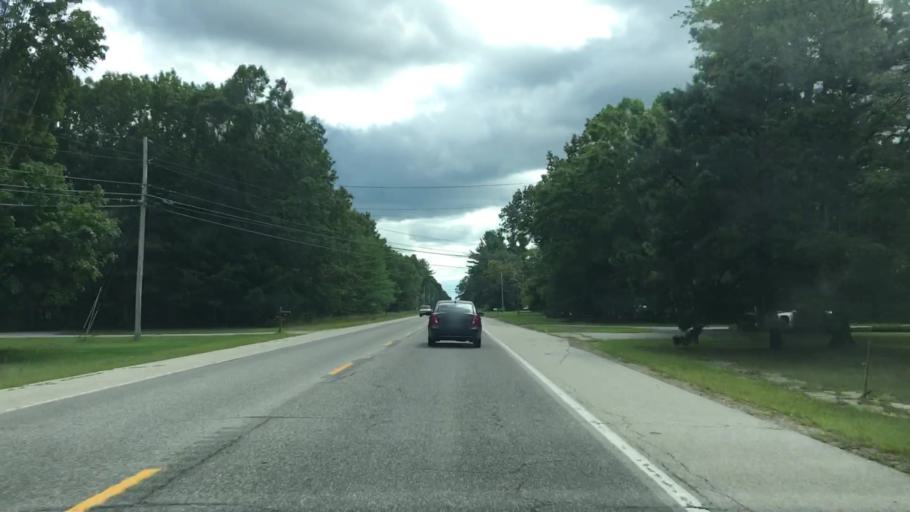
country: US
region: Maine
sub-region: York County
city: North Berwick
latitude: 43.3420
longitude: -70.7318
